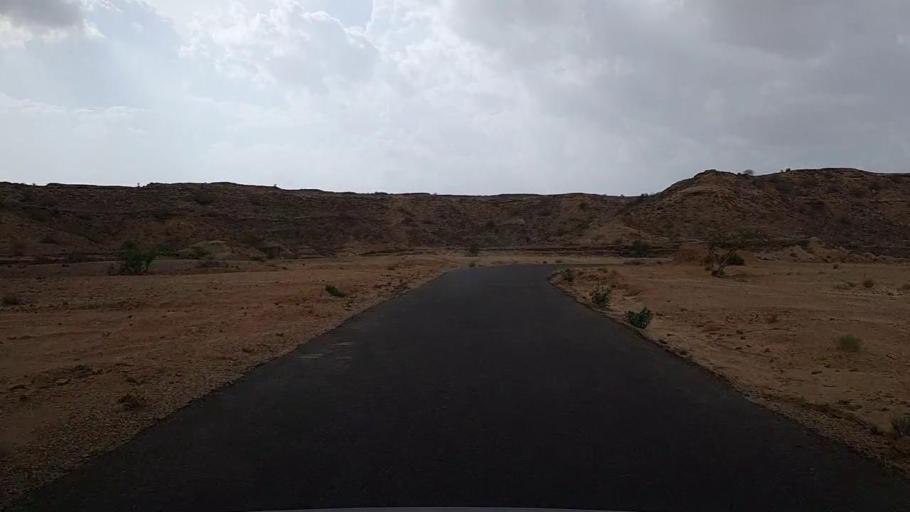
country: PK
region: Sindh
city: Jamshoro
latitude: 25.4224
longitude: 67.6912
